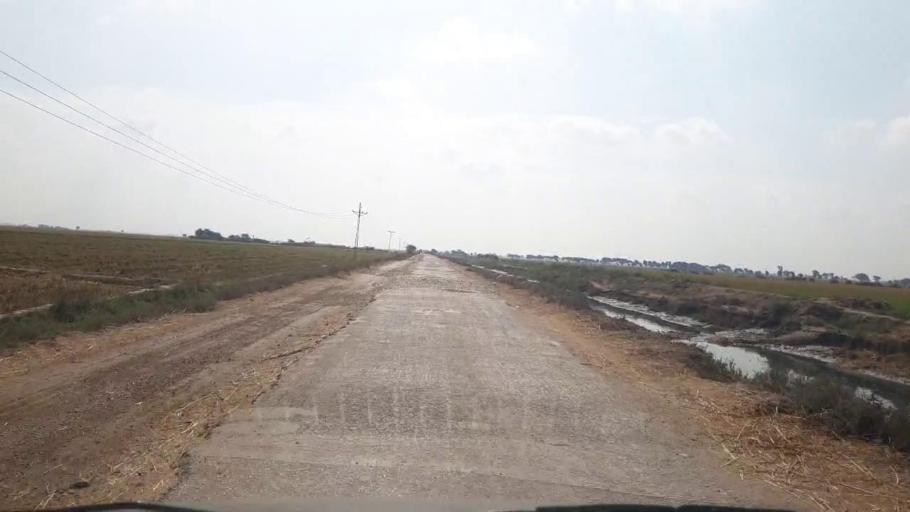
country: PK
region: Sindh
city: Kario
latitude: 24.6319
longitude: 68.5503
